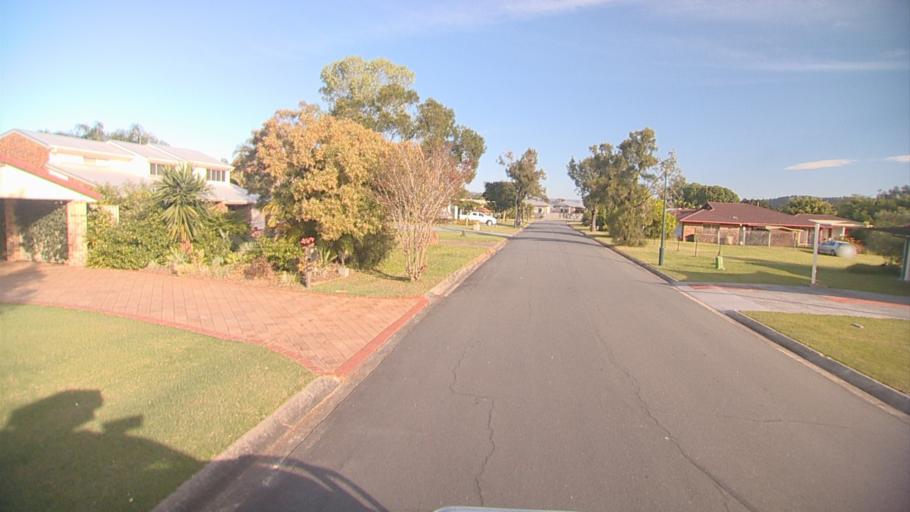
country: AU
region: Queensland
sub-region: Logan
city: Windaroo
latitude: -27.7405
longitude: 153.1981
